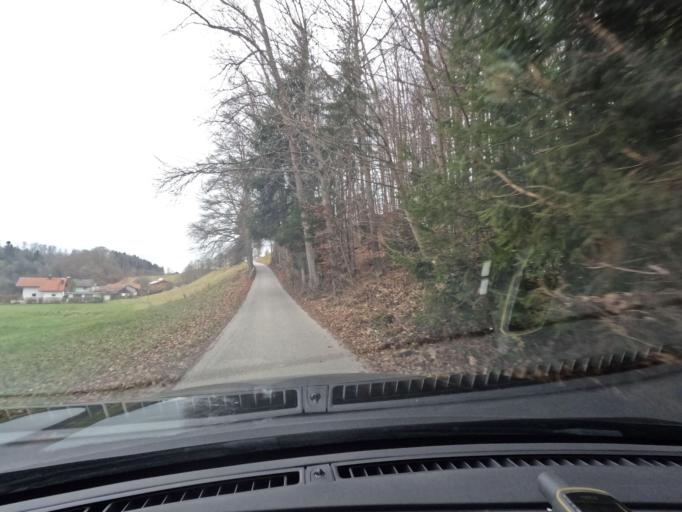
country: DE
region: Bavaria
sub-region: Upper Bavaria
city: Surberg
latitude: 47.8666
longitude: 12.6772
